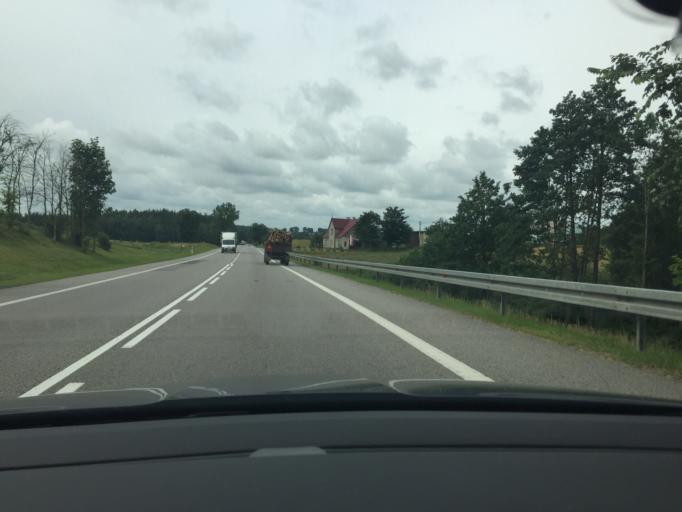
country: PL
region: Pomeranian Voivodeship
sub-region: Powiat starogardzki
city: Smetowo Graniczne
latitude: 53.7422
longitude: 18.7452
